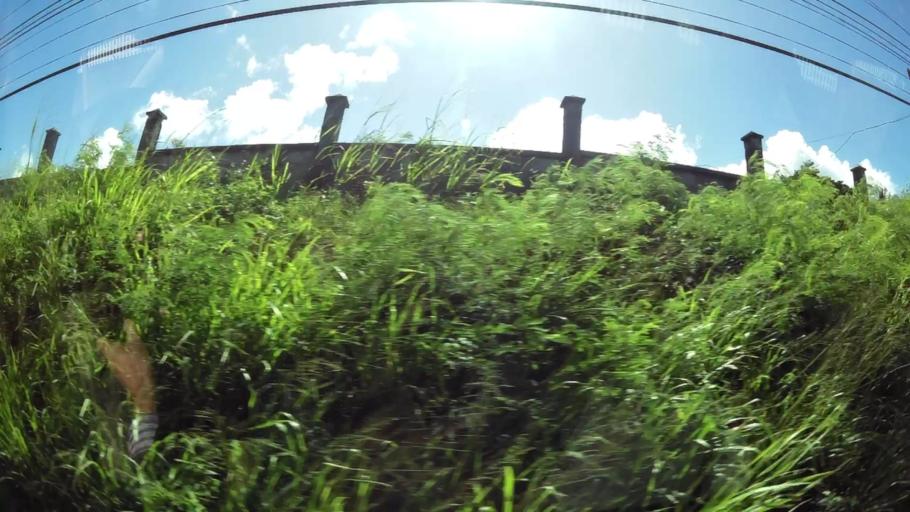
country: GP
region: Guadeloupe
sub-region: Guadeloupe
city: Petit-Canal
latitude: 16.3691
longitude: -61.4421
